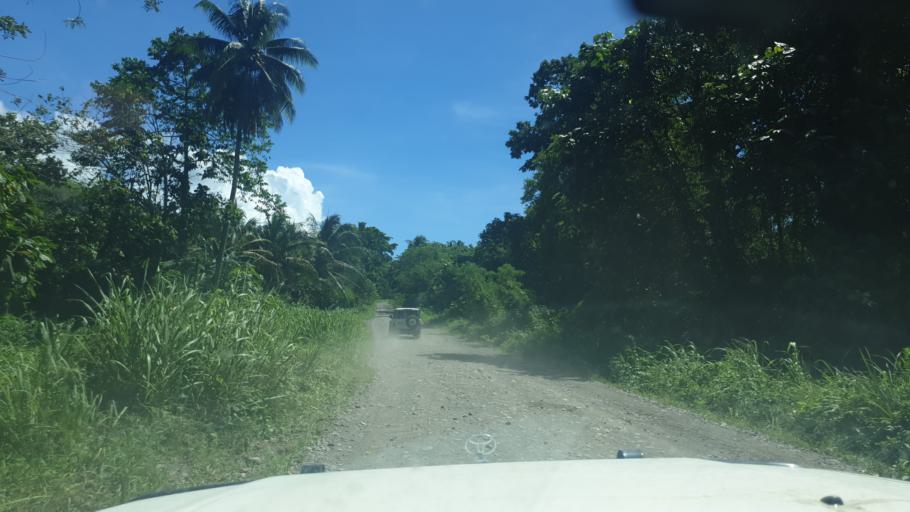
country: PG
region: Bougainville
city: Buka
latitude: -5.6706
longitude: 155.1045
